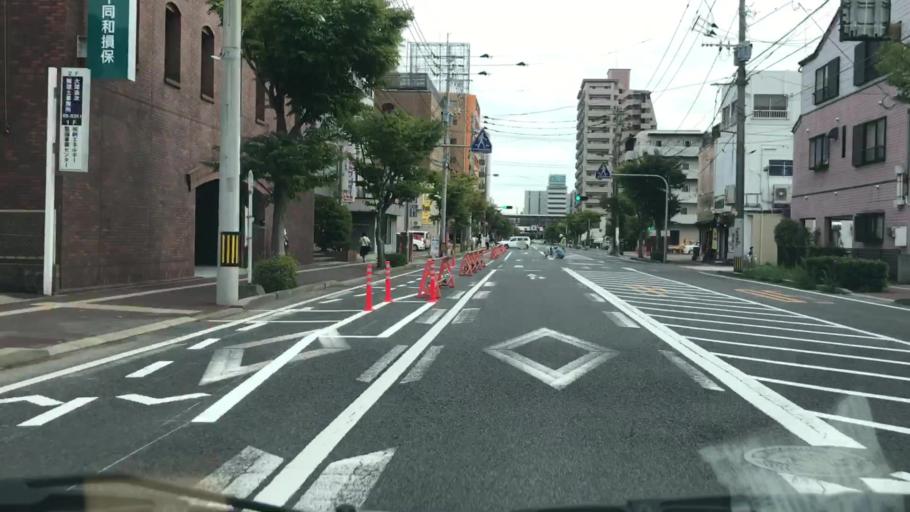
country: JP
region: Saga Prefecture
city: Saga-shi
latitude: 33.2679
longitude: 130.2967
